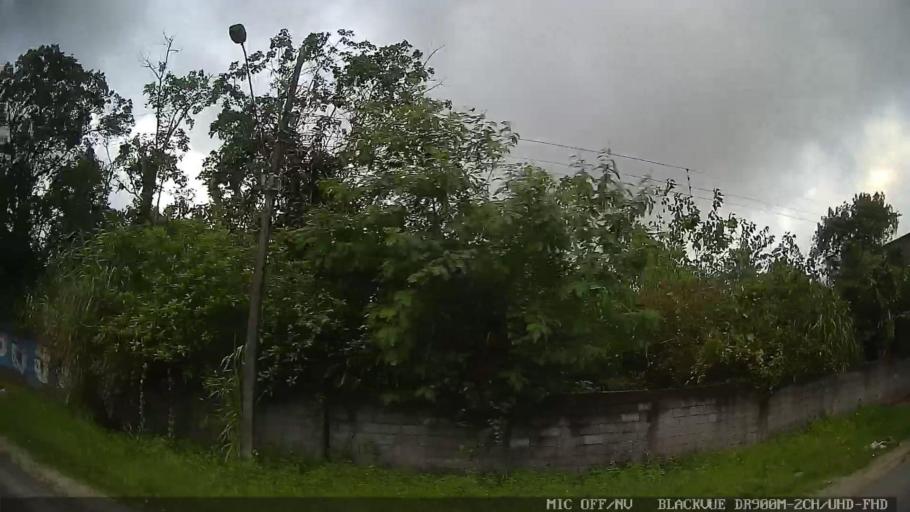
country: BR
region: Sao Paulo
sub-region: Itanhaem
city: Itanhaem
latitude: -24.1574
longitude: -46.7810
